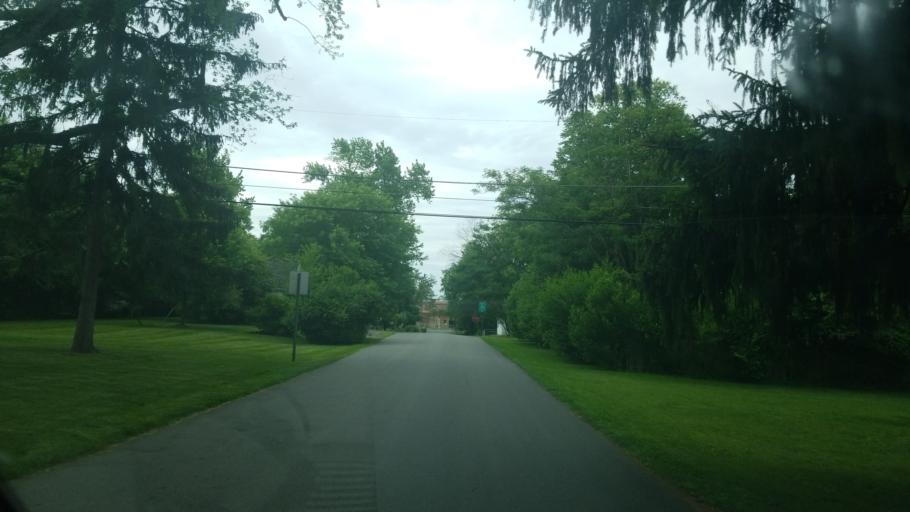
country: US
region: Ohio
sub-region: Franklin County
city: Worthington
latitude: 40.0717
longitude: -83.0122
